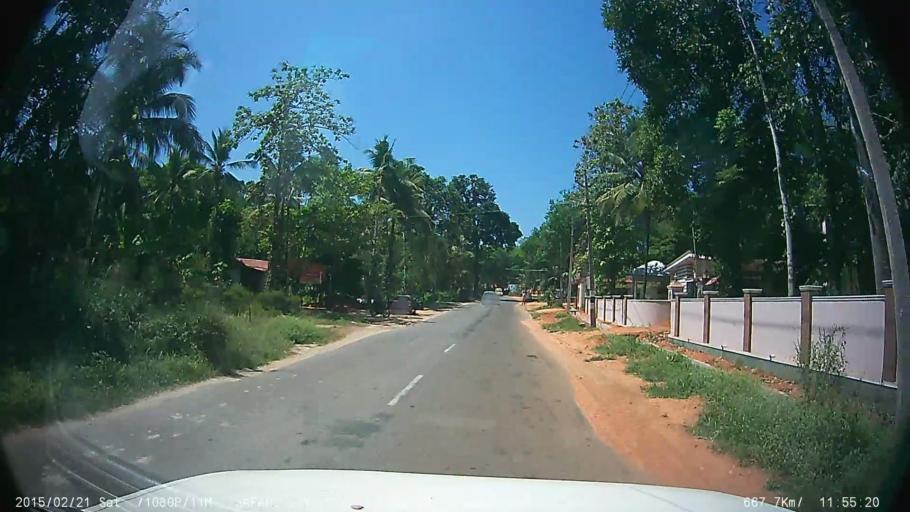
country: IN
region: Kerala
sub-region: Kottayam
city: Lalam
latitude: 9.7445
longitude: 76.7019
